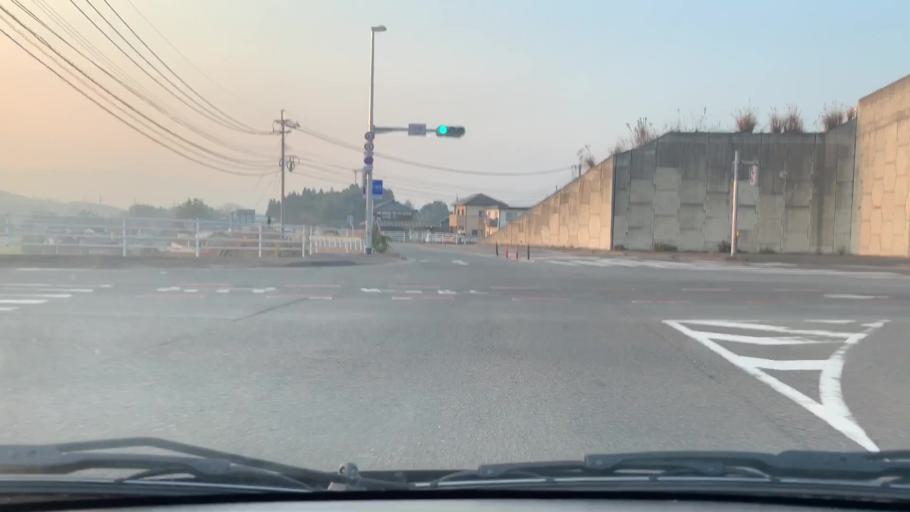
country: JP
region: Saga Prefecture
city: Imaricho-ko
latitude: 33.2644
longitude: 129.9076
